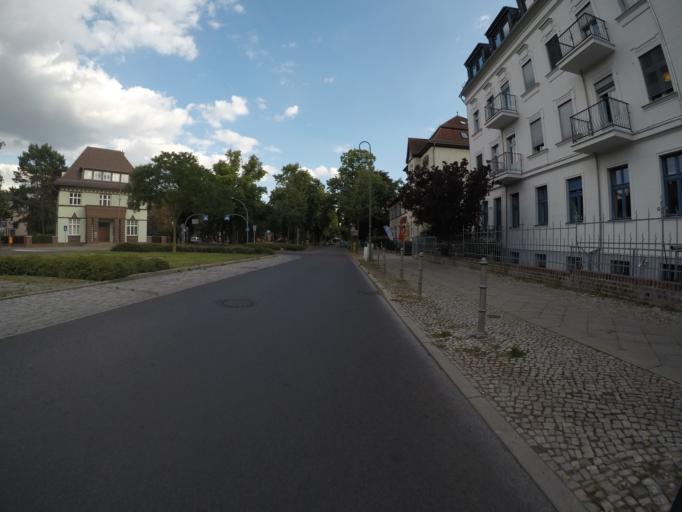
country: DE
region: Berlin
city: Kaulsdorf
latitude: 52.5114
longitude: 13.5872
